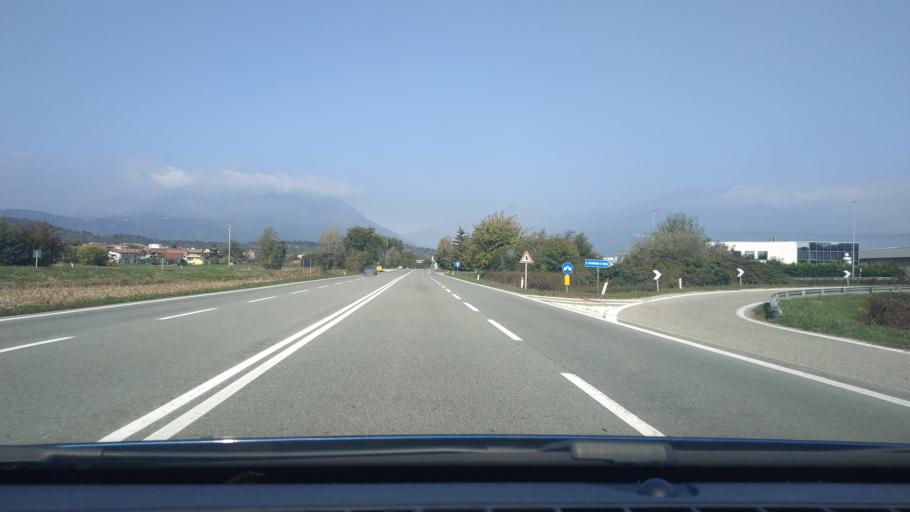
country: IT
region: Piedmont
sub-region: Provincia di Torino
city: Romano Canavese
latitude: 45.4305
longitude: 7.8876
